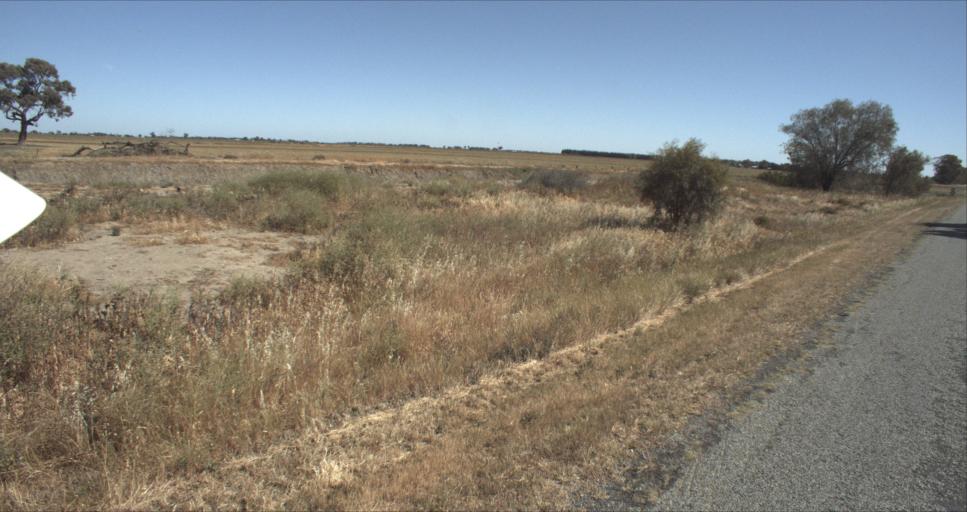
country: AU
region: New South Wales
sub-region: Leeton
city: Leeton
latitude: -34.5406
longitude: 146.3166
